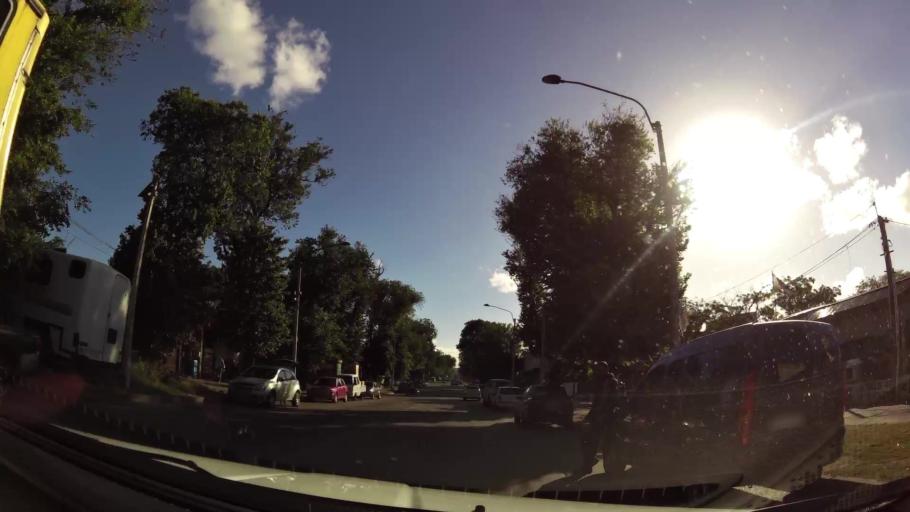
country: UY
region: Montevideo
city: Montevideo
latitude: -34.8641
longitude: -56.2336
